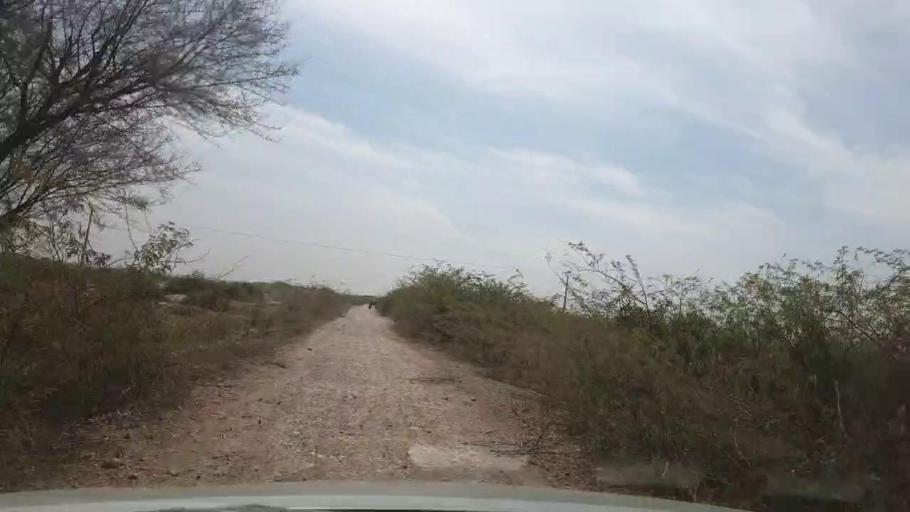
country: PK
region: Sindh
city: Nabisar
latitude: 25.0793
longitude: 69.5988
